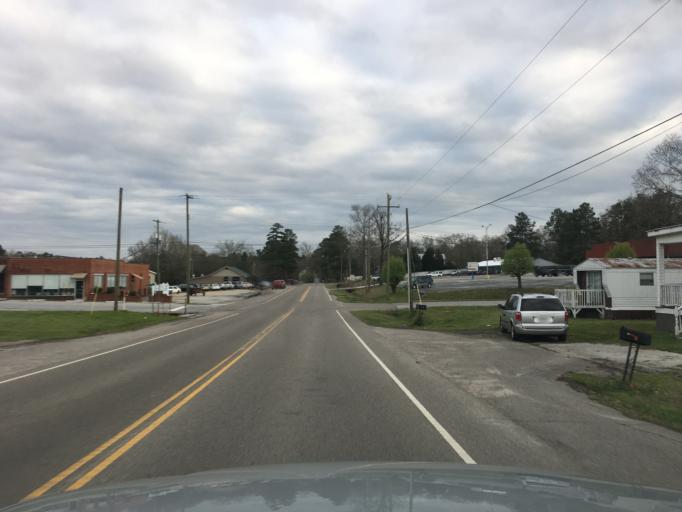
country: US
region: South Carolina
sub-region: Saluda County
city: Saluda
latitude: 34.0008
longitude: -81.7734
